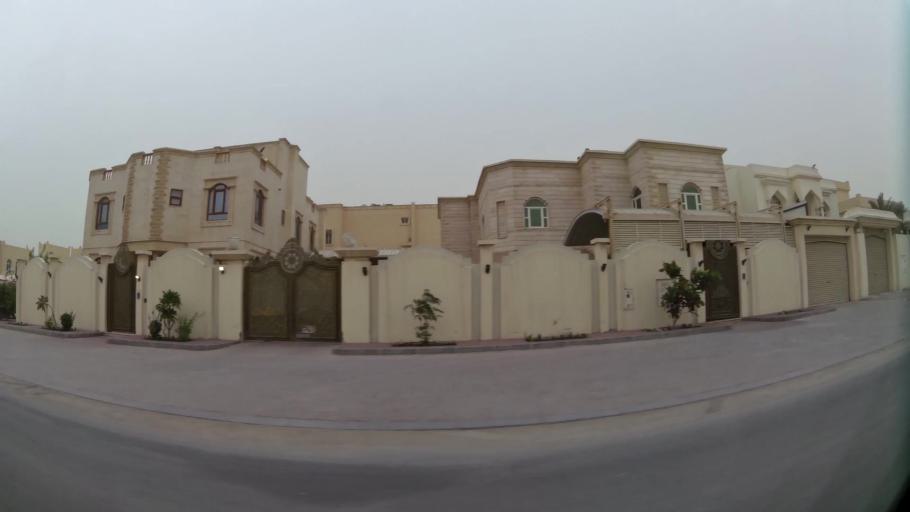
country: QA
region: Baladiyat ad Dawhah
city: Doha
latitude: 25.2367
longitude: 51.4885
